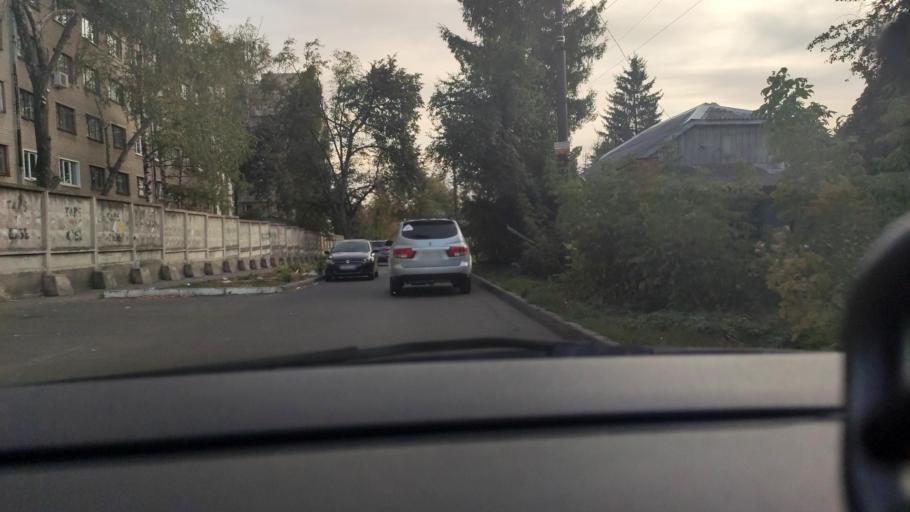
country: RU
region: Voronezj
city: Voronezh
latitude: 51.6866
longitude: 39.2140
